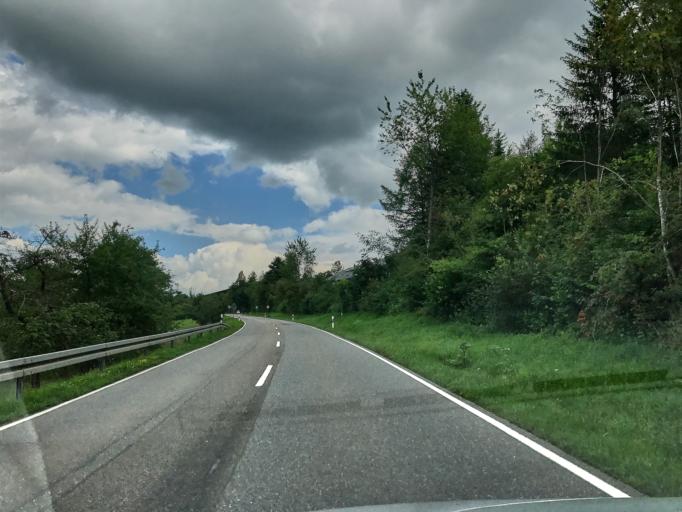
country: DE
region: Baden-Wuerttemberg
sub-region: Karlsruhe Region
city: Lossburg
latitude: 48.4066
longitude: 8.4463
